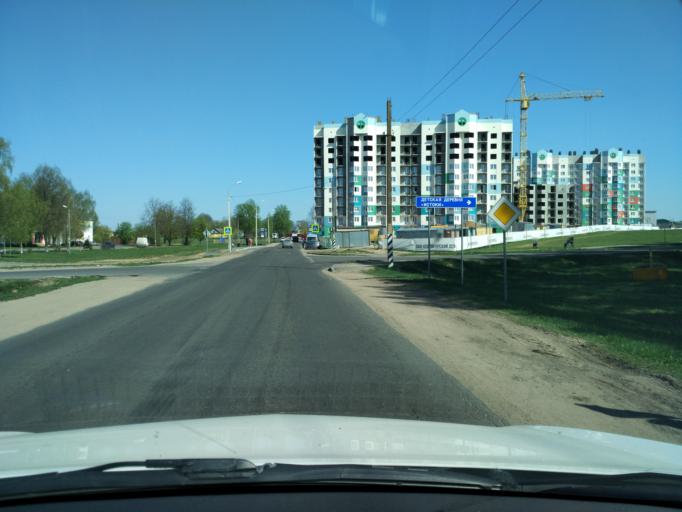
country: BY
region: Minsk
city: Lyeskawka
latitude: 54.0007
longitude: 27.7061
